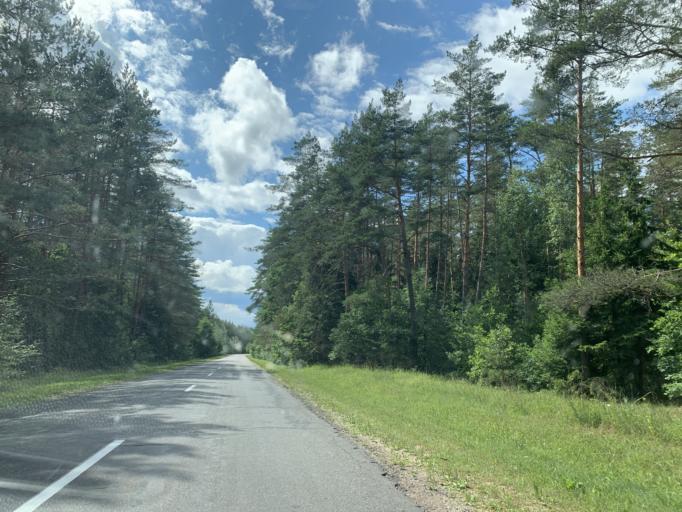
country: BY
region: Minsk
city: Rakaw
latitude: 53.9866
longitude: 26.9405
